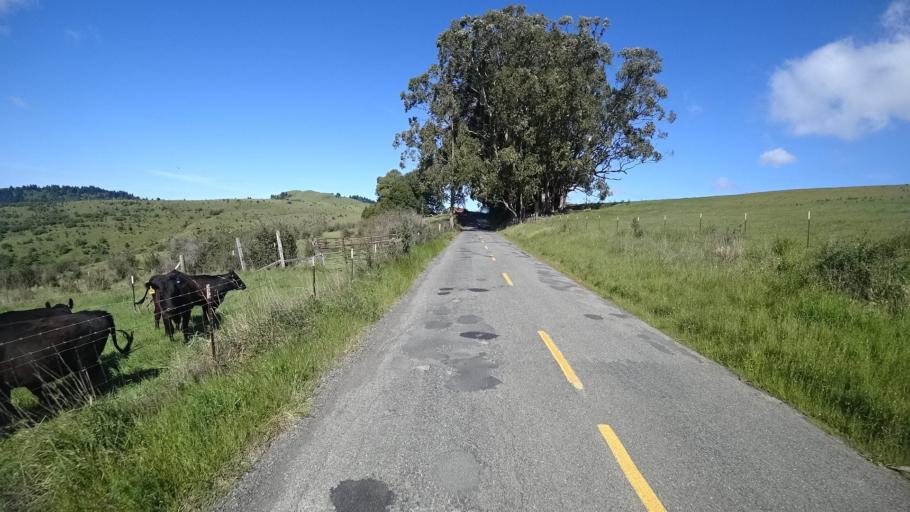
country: US
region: California
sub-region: Humboldt County
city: Ferndale
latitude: 40.3344
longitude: -124.3048
